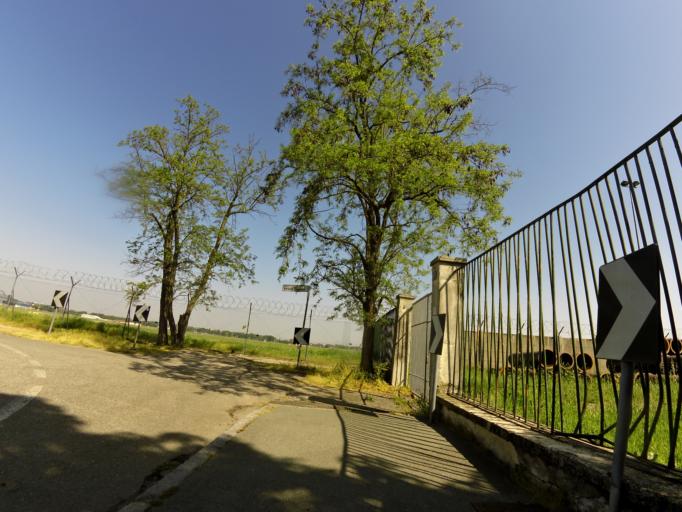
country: IT
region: Lombardy
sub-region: Citta metropolitana di Milano
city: Linate
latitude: 45.4491
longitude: 9.2726
